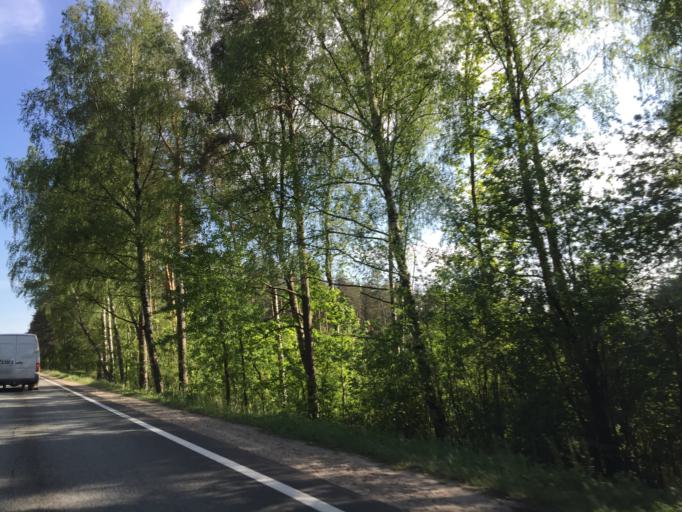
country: LV
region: Riga
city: Bergi
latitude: 56.9481
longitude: 24.3796
